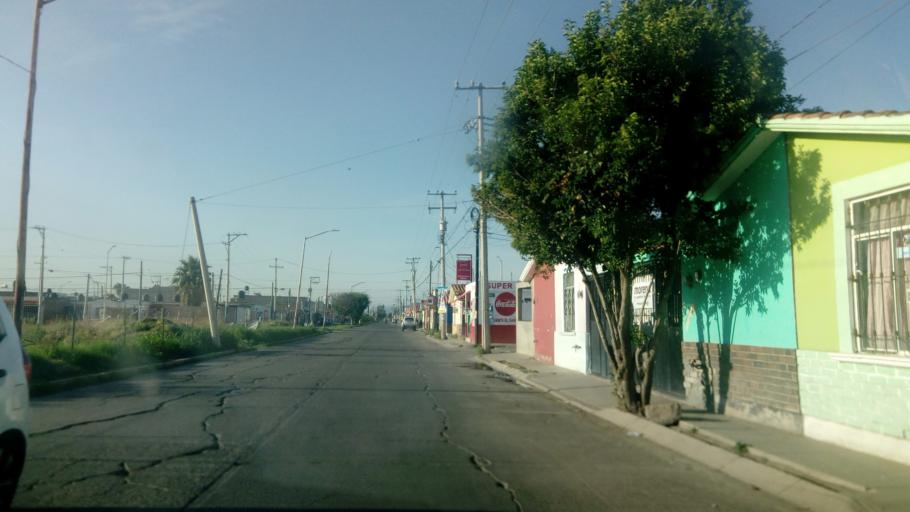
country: MX
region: Durango
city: Victoria de Durango
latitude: 24.0653
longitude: -104.5859
